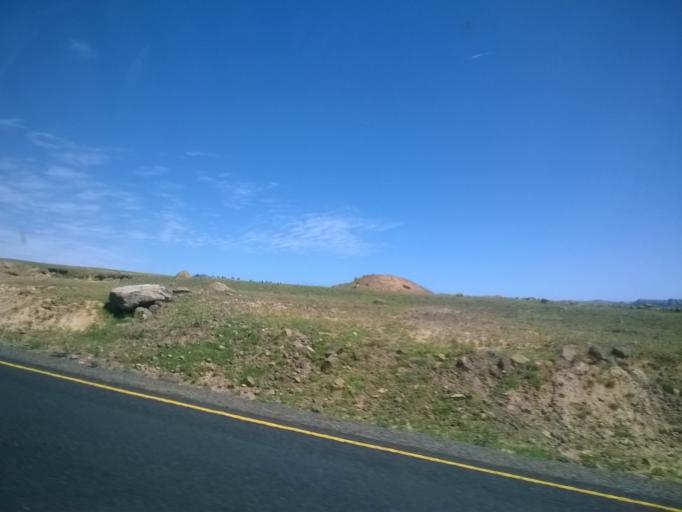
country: LS
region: Berea
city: Teyateyaneng
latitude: -29.0858
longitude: 27.8920
